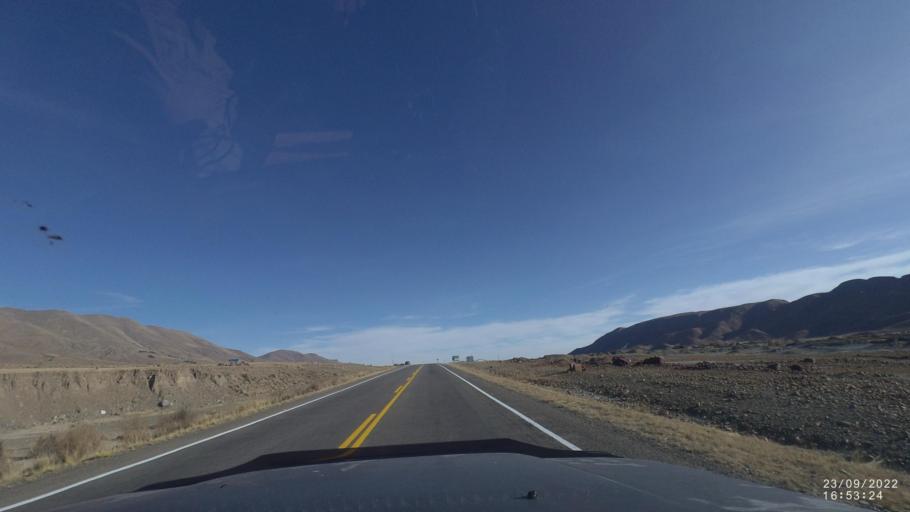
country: BO
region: Oruro
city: Poopo
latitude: -18.4470
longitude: -66.9717
